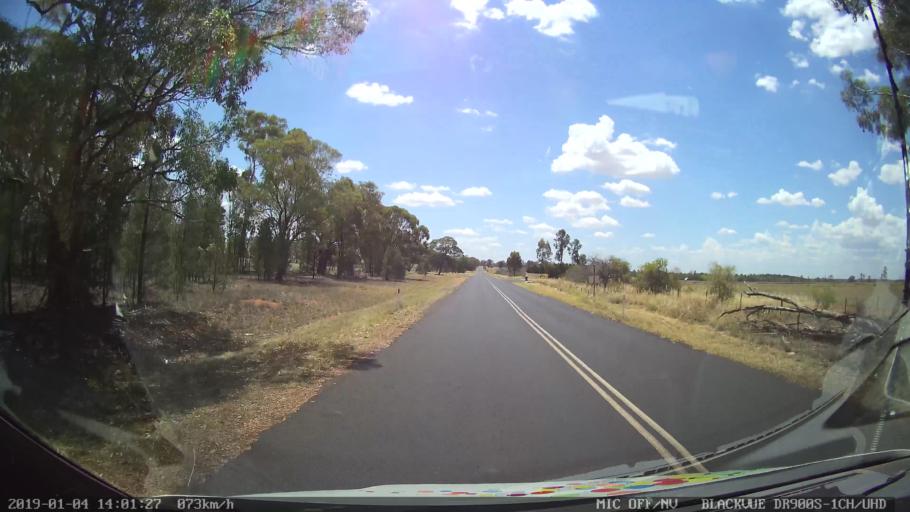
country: AU
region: New South Wales
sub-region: Dubbo Municipality
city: Dubbo
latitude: -32.2966
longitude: 148.5993
